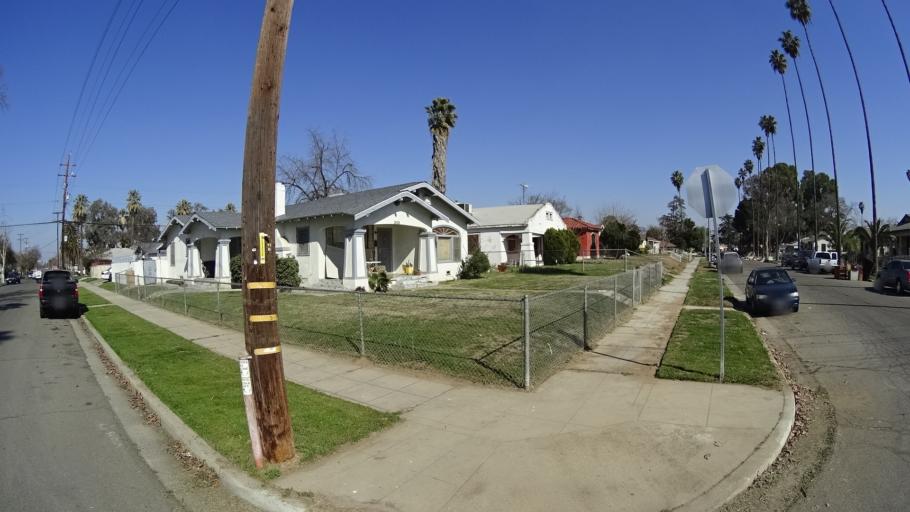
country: US
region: California
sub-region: Fresno County
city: Fresno
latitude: 36.7275
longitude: -119.8087
